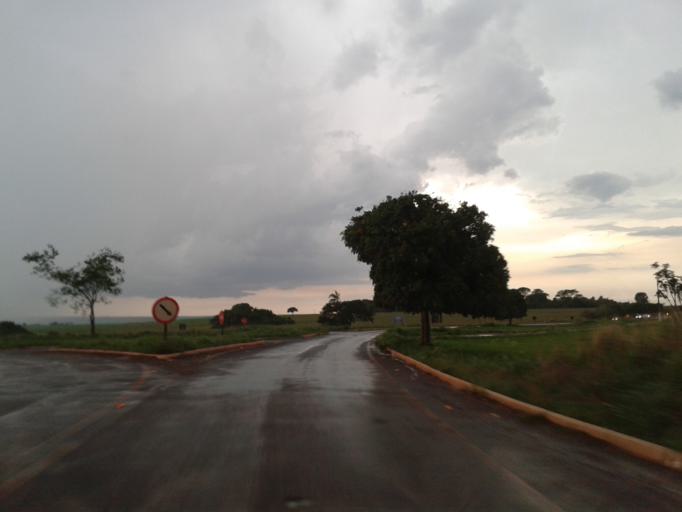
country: BR
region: Goias
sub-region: Quirinopolis
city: Quirinopolis
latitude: -18.4438
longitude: -50.4150
